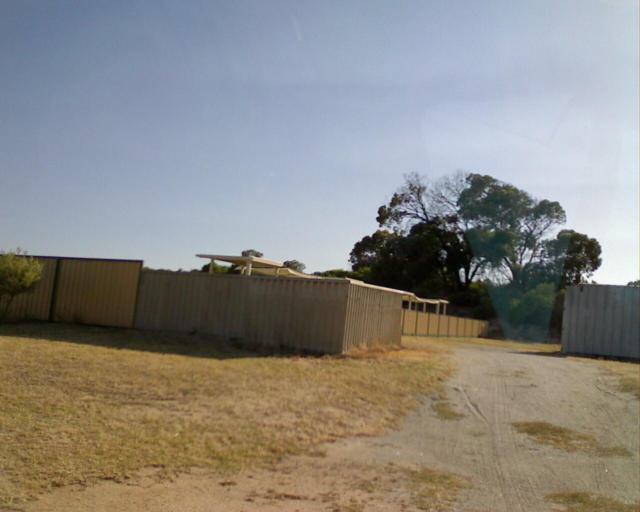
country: AU
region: Western Australia
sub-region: Dandaragan
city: Jurien Bay
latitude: -30.0669
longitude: 114.9723
